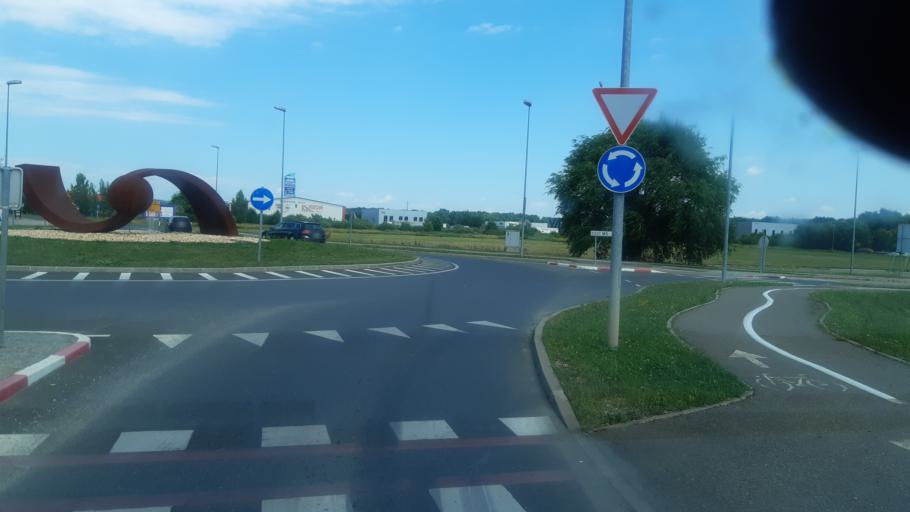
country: SI
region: Murska Sobota
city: Murska Sobota
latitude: 46.6700
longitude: 16.1798
